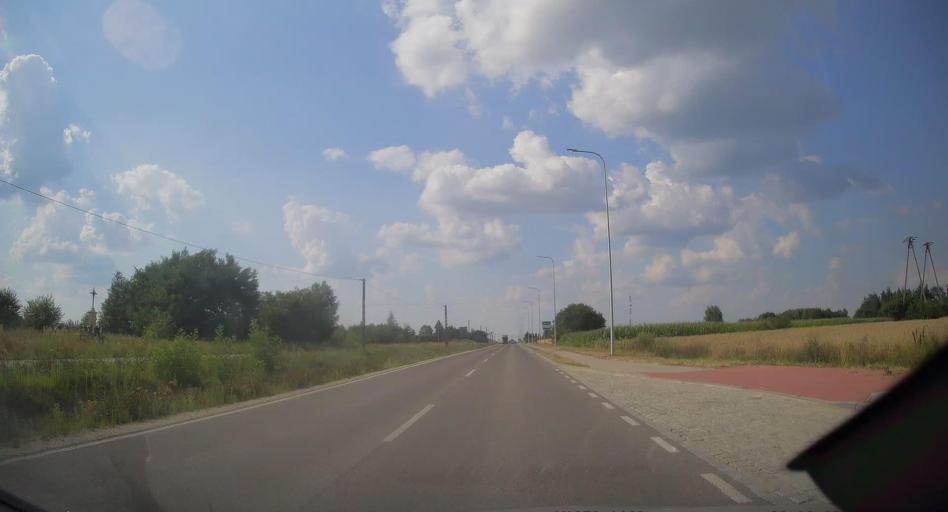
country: PL
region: Swietokrzyskie
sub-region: Powiat konecki
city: Radoszyce
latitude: 51.0659
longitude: 20.2721
